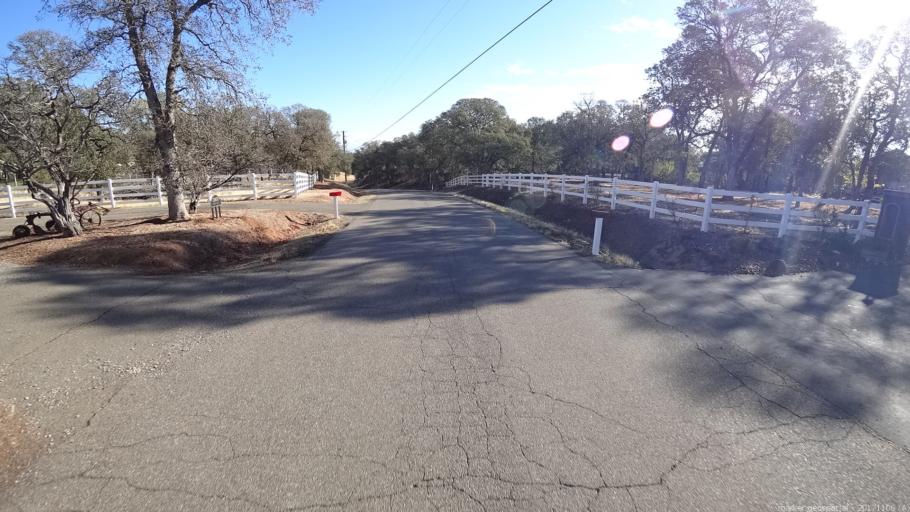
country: US
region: California
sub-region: Shasta County
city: Palo Cedro
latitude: 40.5110
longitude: -122.2433
